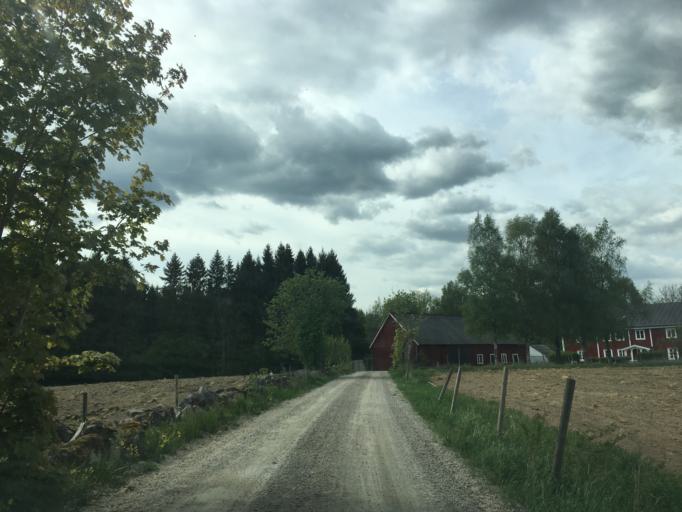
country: SE
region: Blekinge
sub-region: Olofstroms Kommun
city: Olofstroem
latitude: 56.4017
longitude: 14.5814
